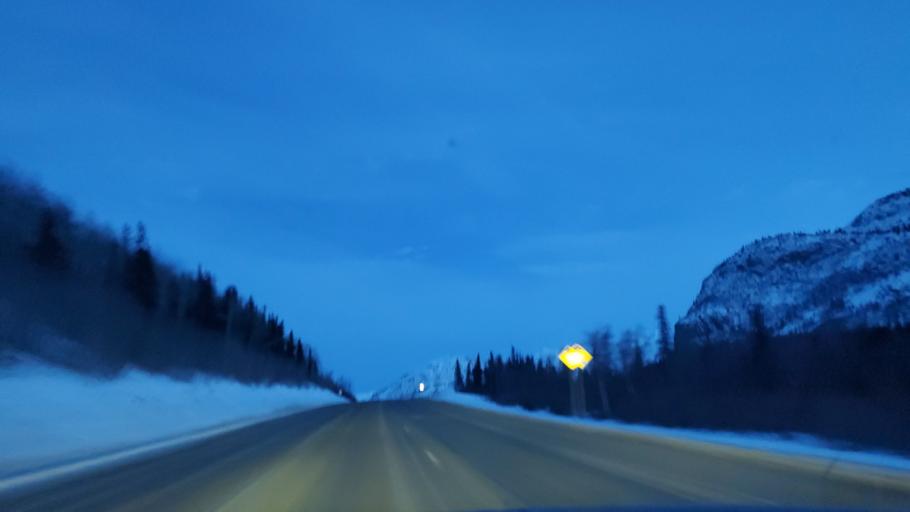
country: US
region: Alaska
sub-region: Matanuska-Susitna Borough
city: Sutton-Alpine
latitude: 61.7914
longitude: -147.6866
